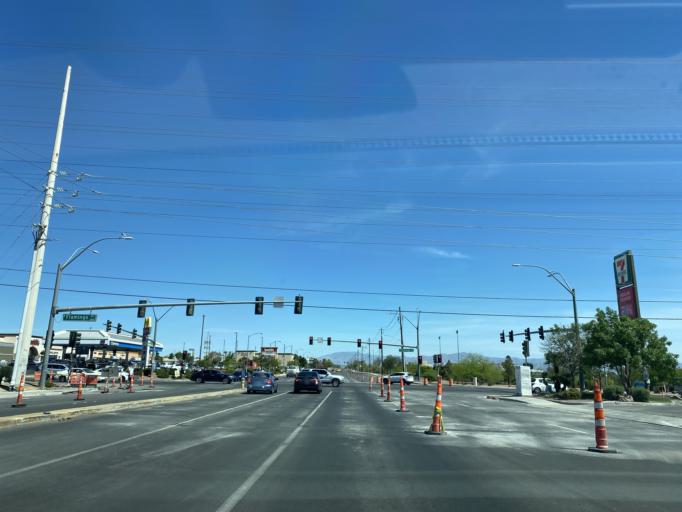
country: US
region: Nevada
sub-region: Clark County
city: Spring Valley
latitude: 36.1140
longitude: -115.2609
